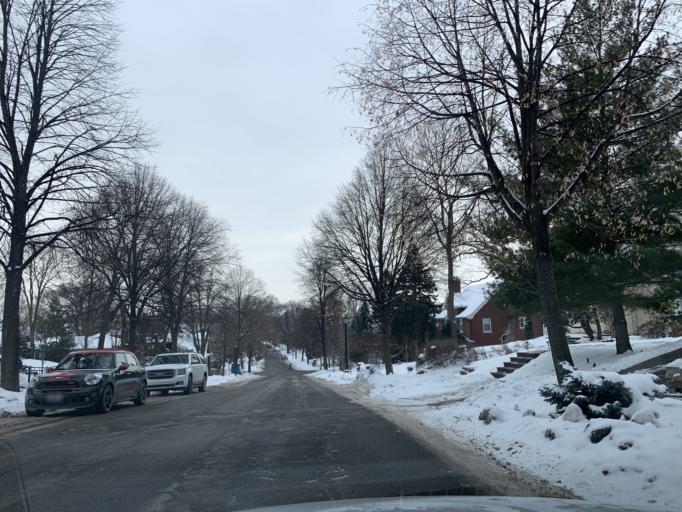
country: US
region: Minnesota
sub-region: Hennepin County
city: Minneapolis
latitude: 44.9620
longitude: -93.2996
